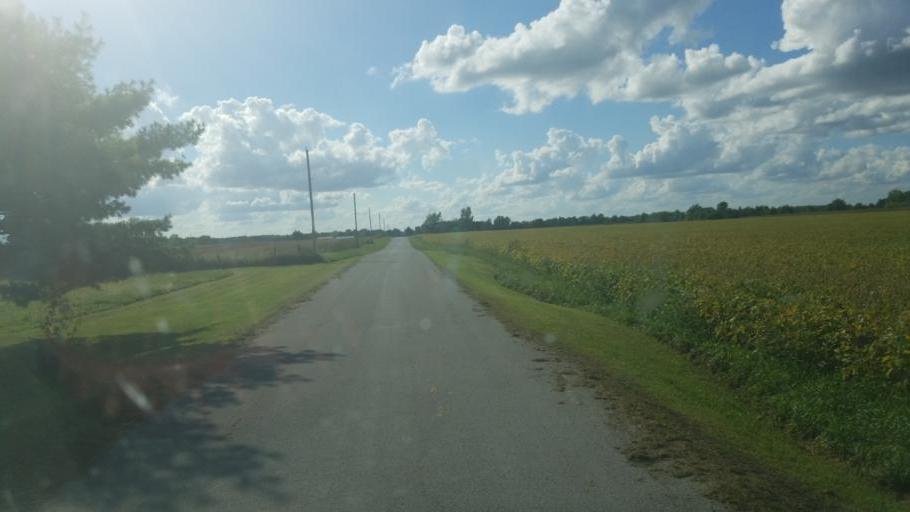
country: US
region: Ohio
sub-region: Hardin County
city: Ada
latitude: 40.7184
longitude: -83.7248
